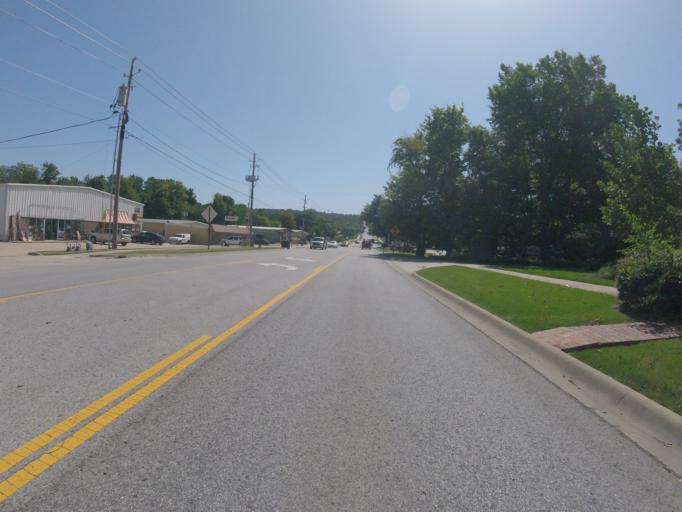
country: US
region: Arkansas
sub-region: Washington County
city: Fayetteville
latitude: 36.0954
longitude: -94.1589
